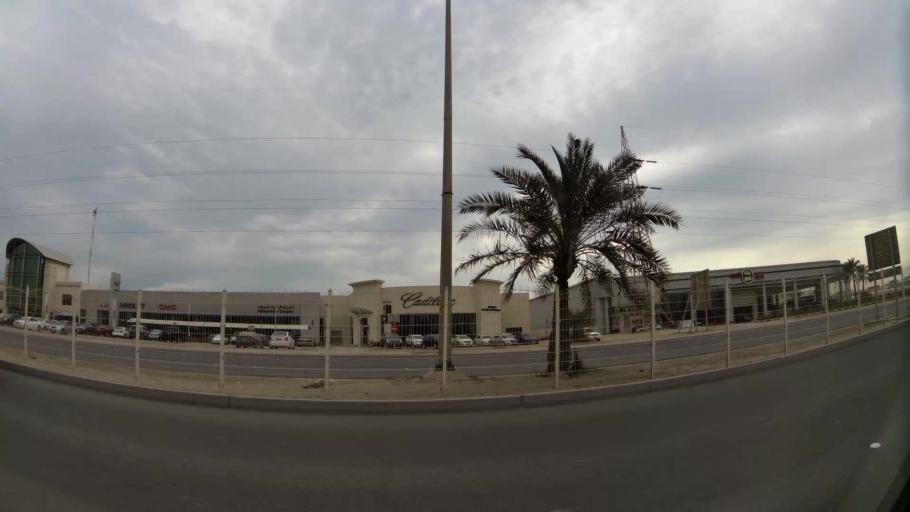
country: BH
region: Northern
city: Sitrah
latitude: 26.1688
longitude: 50.6038
